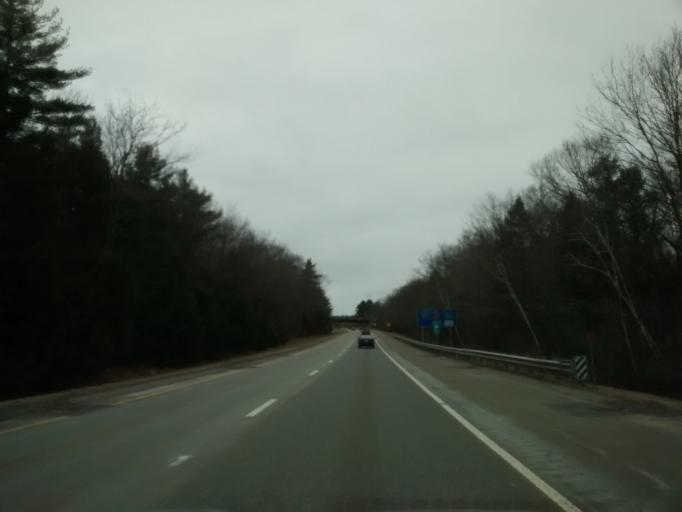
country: US
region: Massachusetts
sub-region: Worcester County
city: Templeton
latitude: 42.5626
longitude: -72.0541
